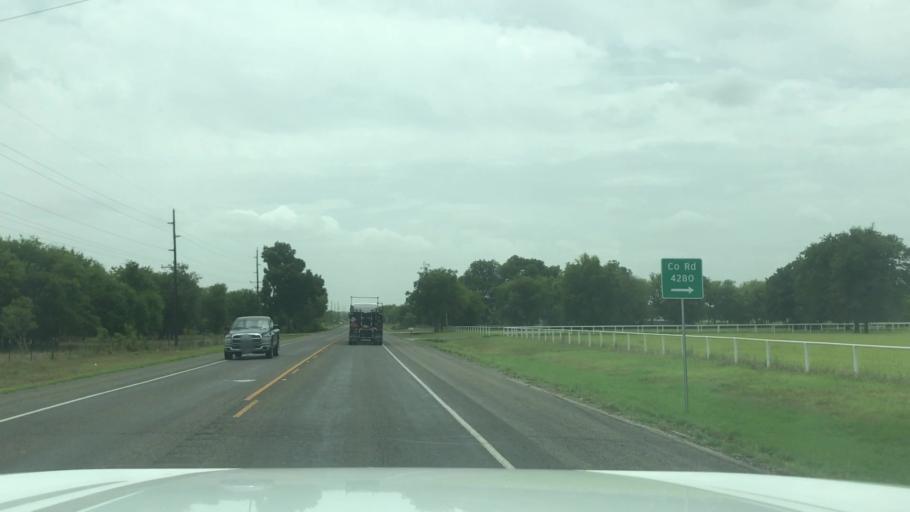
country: US
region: Texas
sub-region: Bosque County
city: Clifton
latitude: 31.7384
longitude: -97.5519
